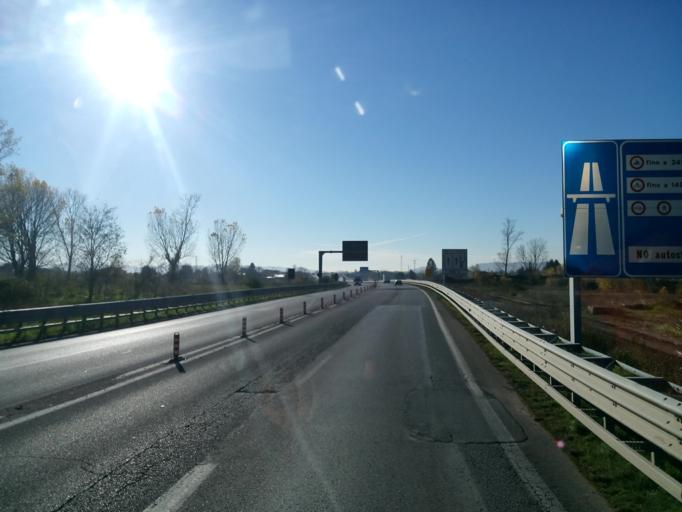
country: IT
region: Veneto
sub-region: Provincia di Vicenza
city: Tezze
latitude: 45.5179
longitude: 11.3871
